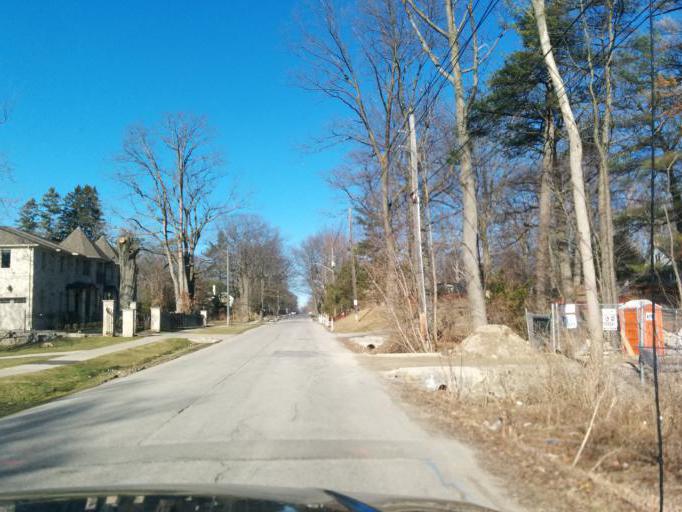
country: CA
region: Ontario
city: Mississauga
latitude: 43.5561
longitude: -79.5968
